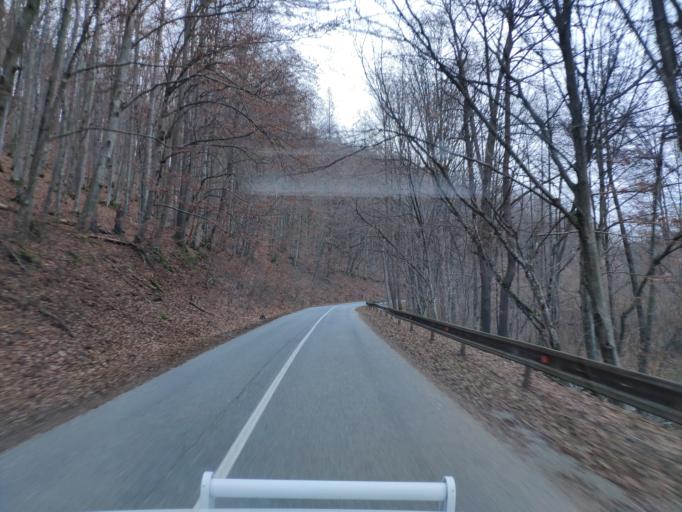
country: SK
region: Kosicky
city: Dobsina
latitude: 48.7781
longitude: 20.4757
